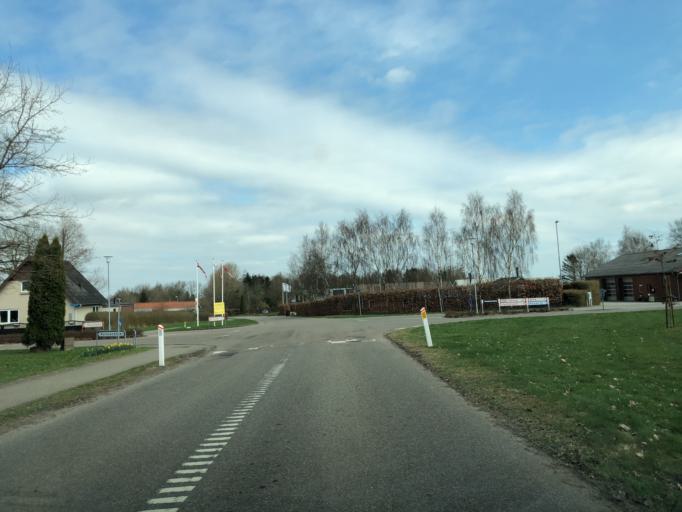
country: DK
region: South Denmark
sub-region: Vejle Kommune
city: Give
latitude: 55.9068
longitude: 9.2653
